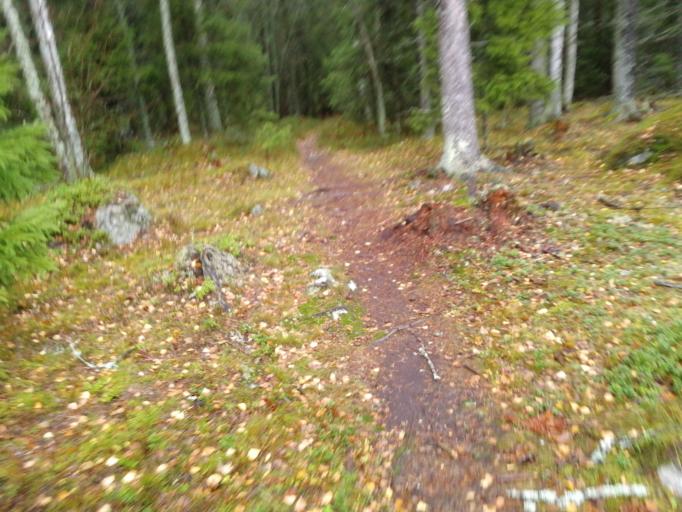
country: FI
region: Pirkanmaa
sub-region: Tampere
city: Tampere
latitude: 61.4561
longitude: 23.8835
